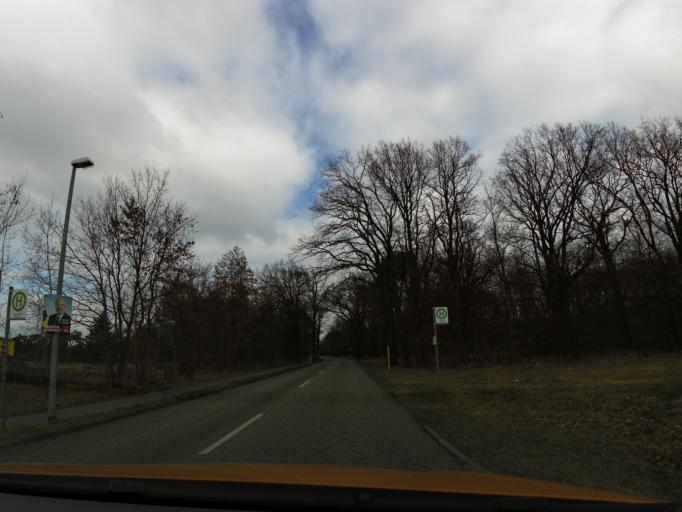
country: DE
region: Brandenburg
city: Rathenow
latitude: 52.6296
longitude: 12.3546
